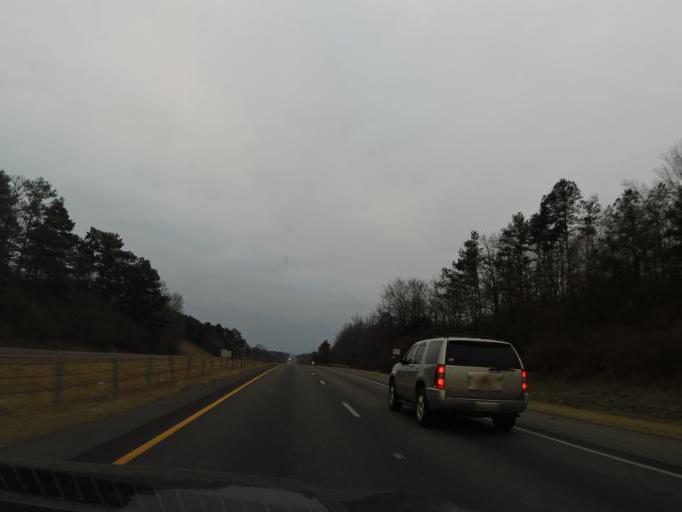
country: US
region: Alabama
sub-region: Cullman County
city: Good Hope
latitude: 34.1055
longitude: -86.8663
